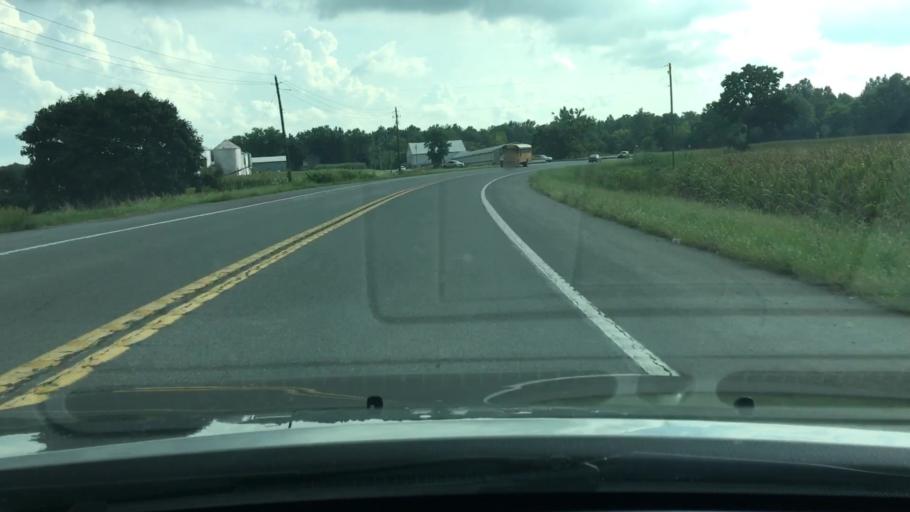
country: US
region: Pennsylvania
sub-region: Franklin County
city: Scotland
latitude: 39.9427
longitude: -77.5832
